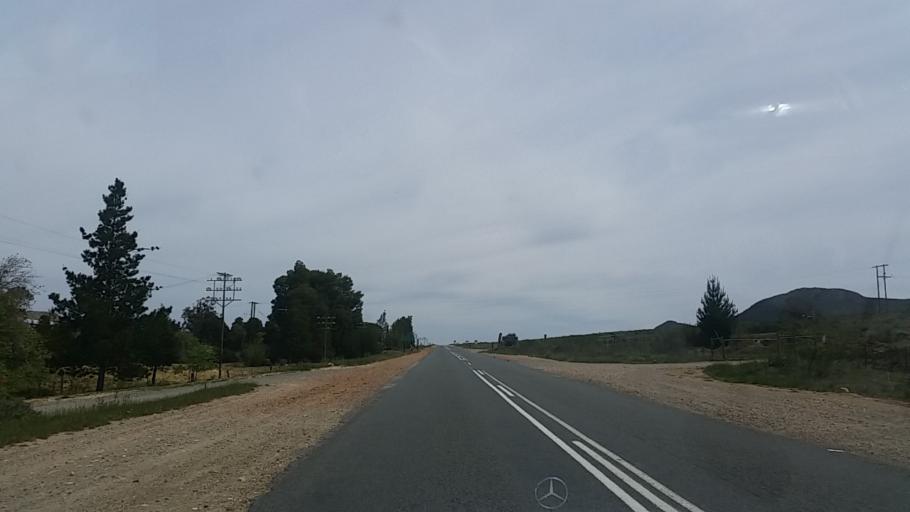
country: ZA
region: Western Cape
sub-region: Eden District Municipality
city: Knysna
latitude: -33.7694
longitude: 22.7895
